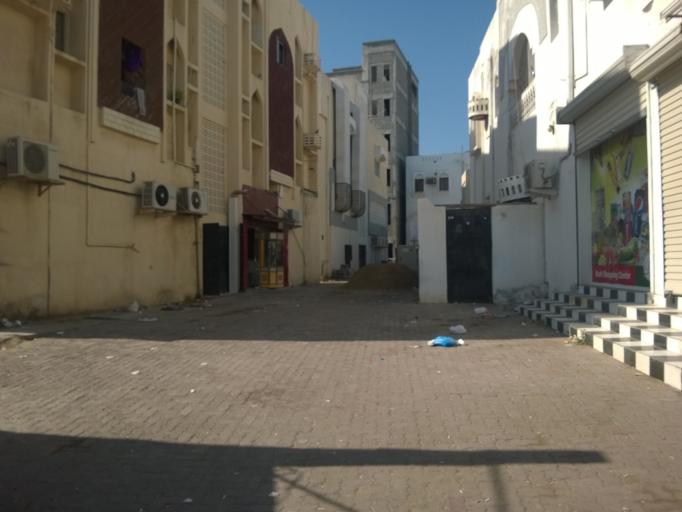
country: OM
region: Muhafazat Masqat
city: As Sib al Jadidah
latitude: 23.6778
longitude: 58.1900
